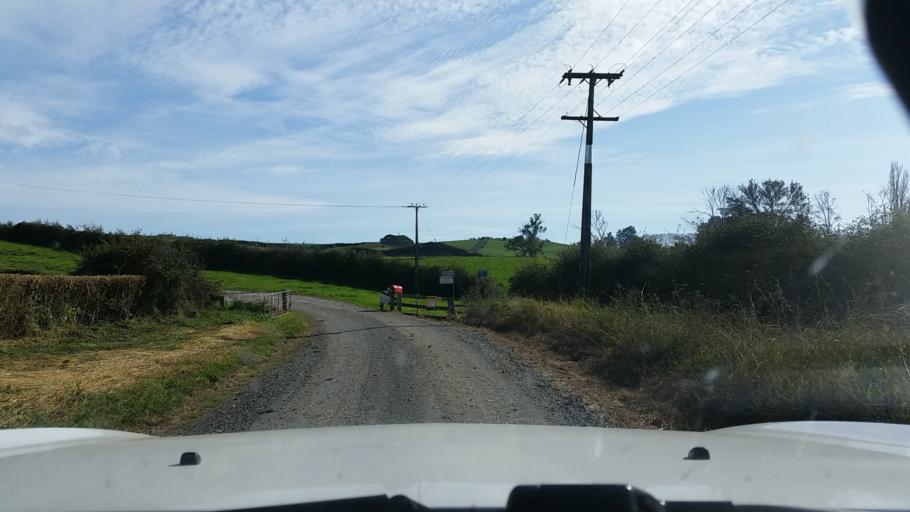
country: NZ
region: Waikato
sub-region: Matamata-Piako District
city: Matamata
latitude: -37.7578
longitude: 175.6195
